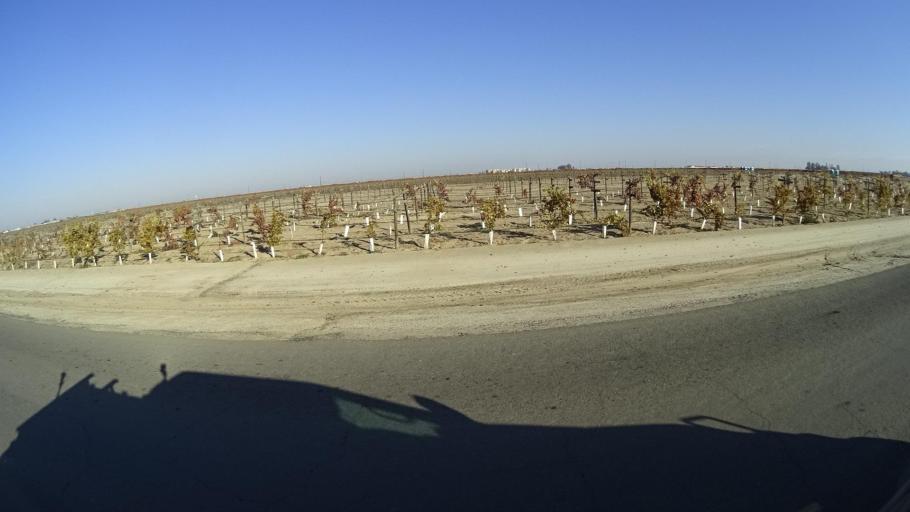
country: US
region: California
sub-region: Kern County
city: Delano
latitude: 35.7686
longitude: -119.1930
